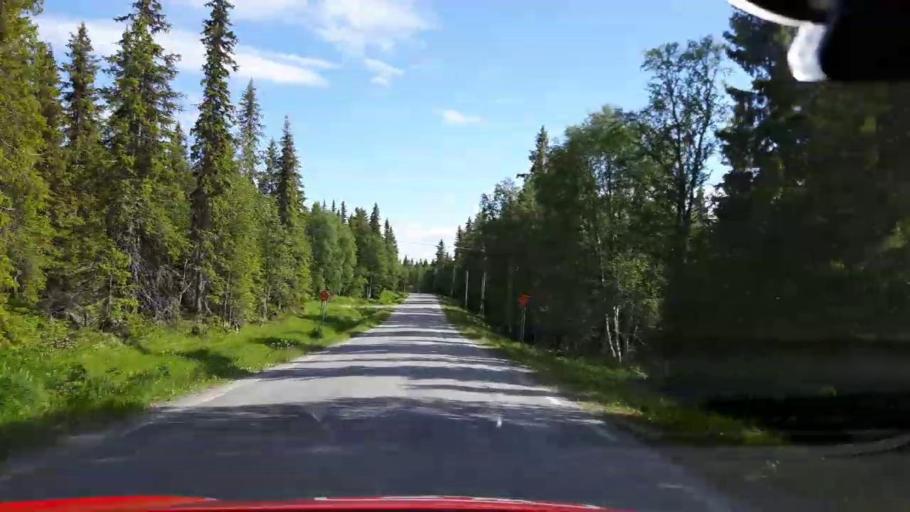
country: SE
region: Jaemtland
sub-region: Krokoms Kommun
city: Valla
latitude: 63.7742
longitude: 14.0462
